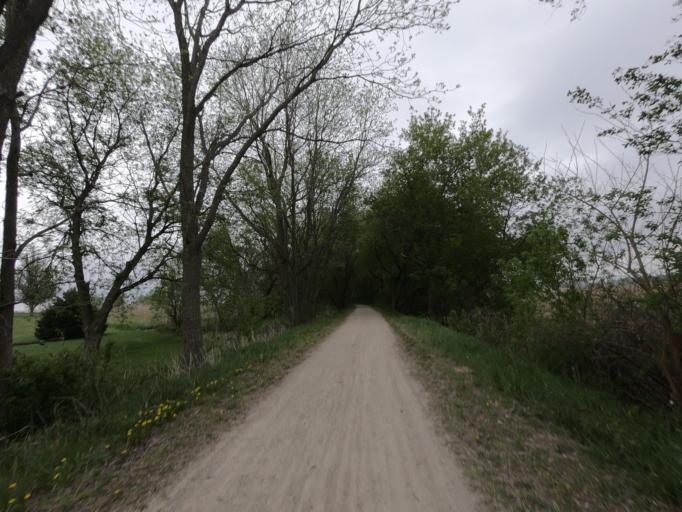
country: US
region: Wisconsin
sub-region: Jefferson County
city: Lake Mills
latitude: 43.0509
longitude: -88.8701
